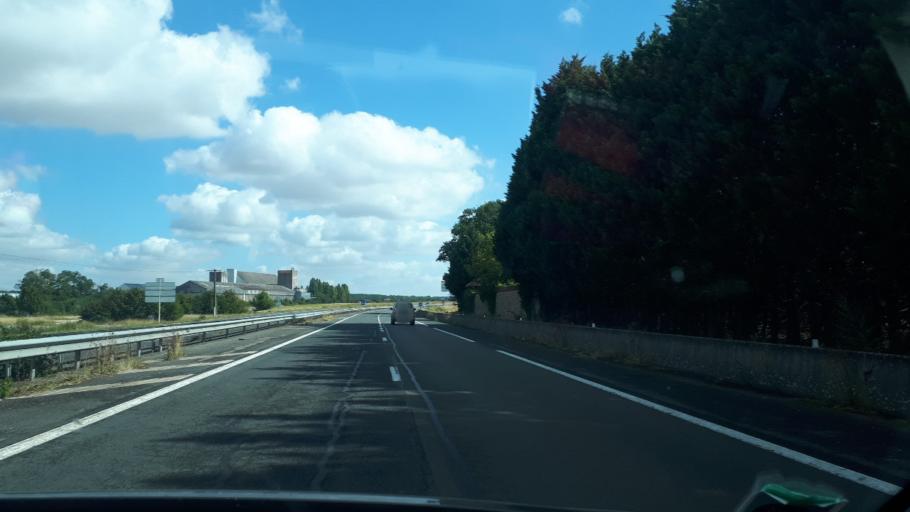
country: FR
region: Centre
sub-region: Departement du Loir-et-Cher
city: Saint-Ouen
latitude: 47.8422
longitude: 1.0917
